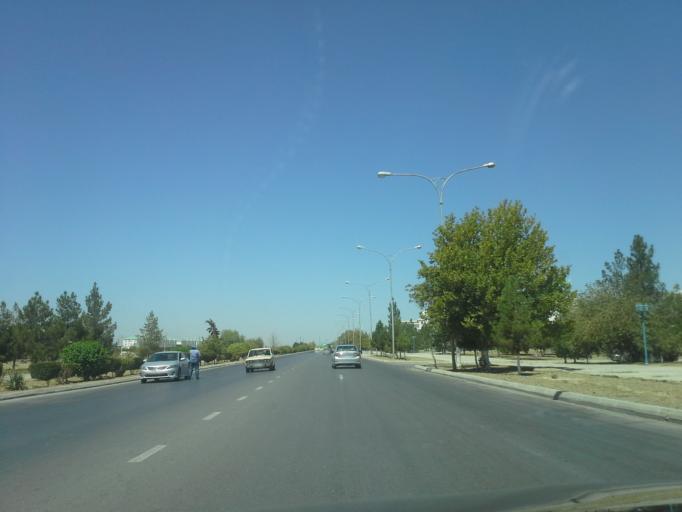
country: TM
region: Ahal
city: Ashgabat
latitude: 37.9881
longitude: 58.3279
